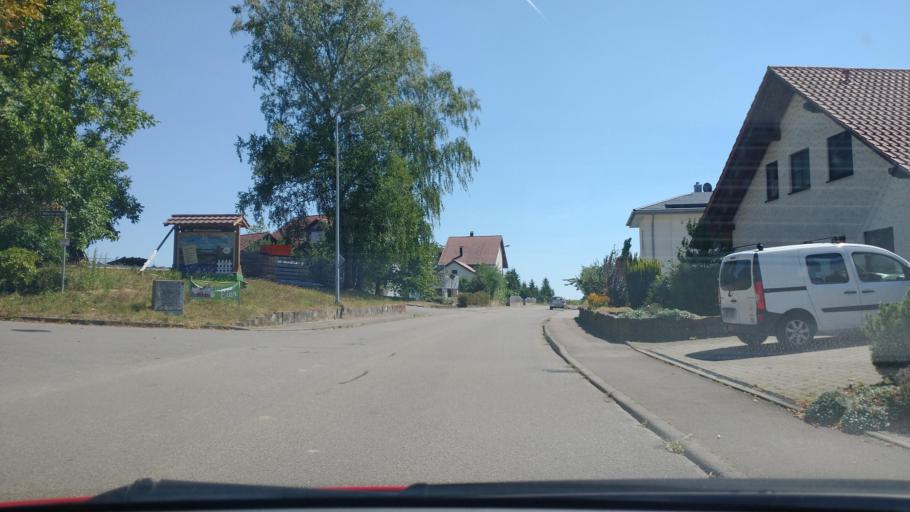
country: DE
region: Baden-Wuerttemberg
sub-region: Regierungsbezirk Stuttgart
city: Alfdorf
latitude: 48.8350
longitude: 9.6884
